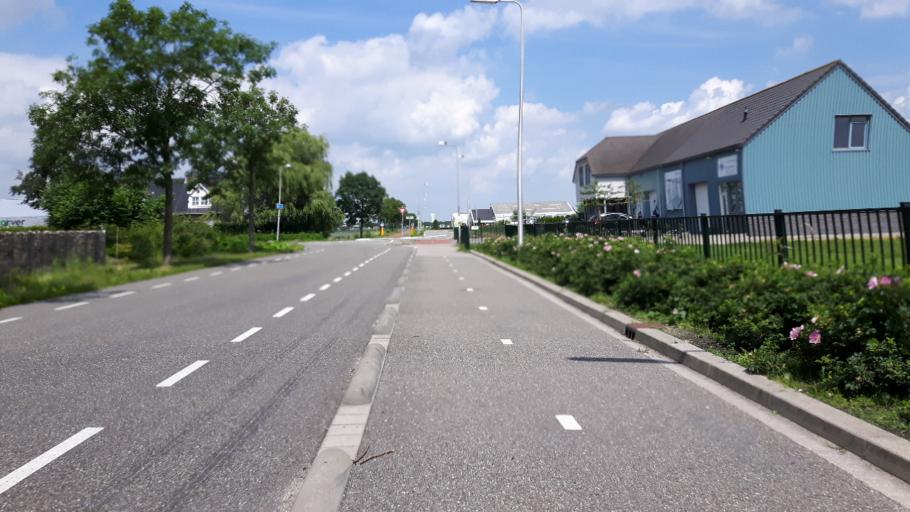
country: NL
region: South Holland
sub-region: Gemeente Boskoop
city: Boskoop
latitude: 52.0906
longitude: 4.6836
